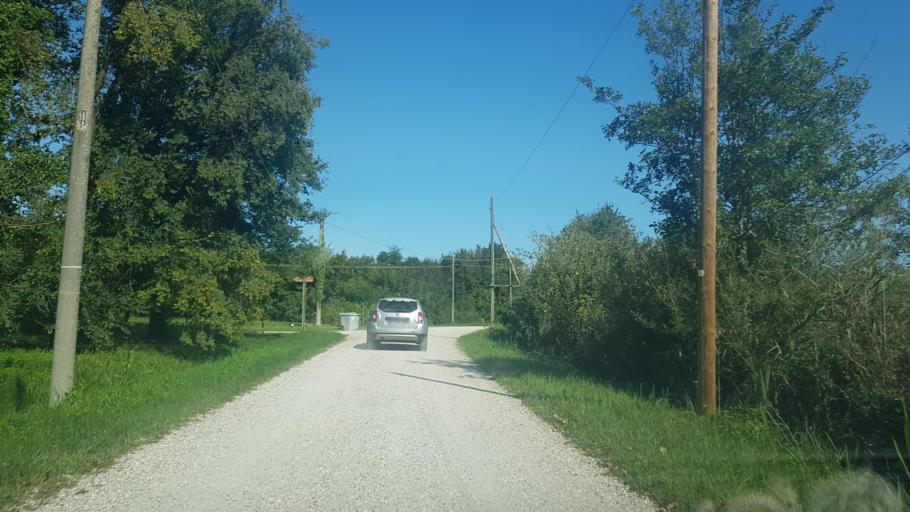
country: IT
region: Friuli Venezia Giulia
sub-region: Provincia di Udine
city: Gonars
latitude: 45.8806
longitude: 13.2264
